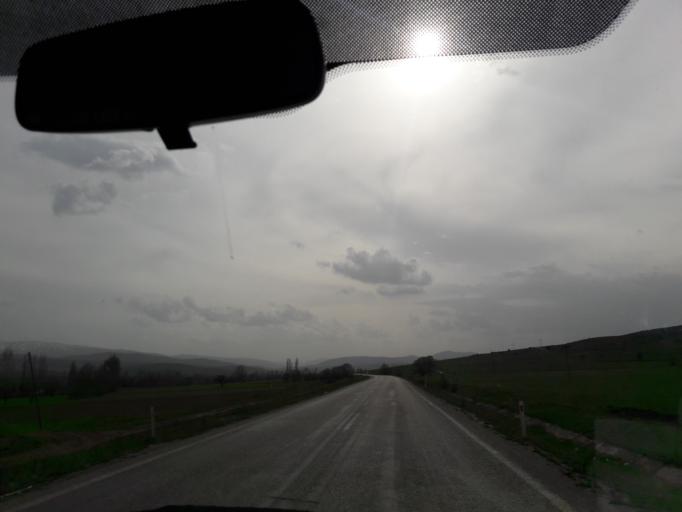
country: TR
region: Gumushane
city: Siran
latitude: 40.1713
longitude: 39.0749
